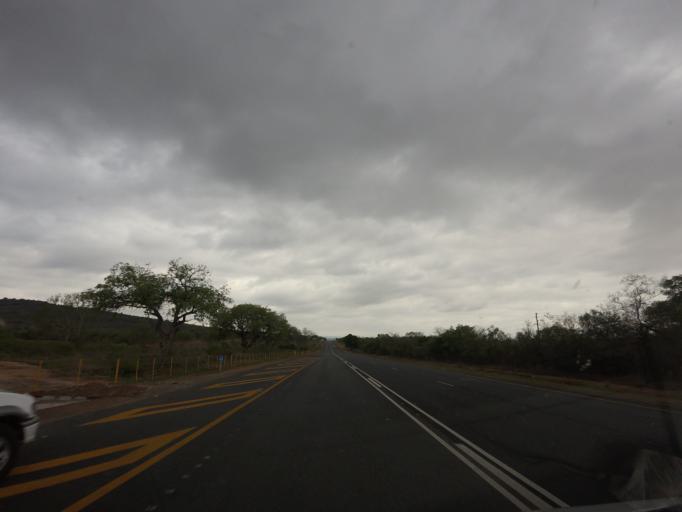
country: ZA
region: Mpumalanga
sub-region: Ehlanzeni District
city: Komatipoort
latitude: -25.4395
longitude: 31.7730
